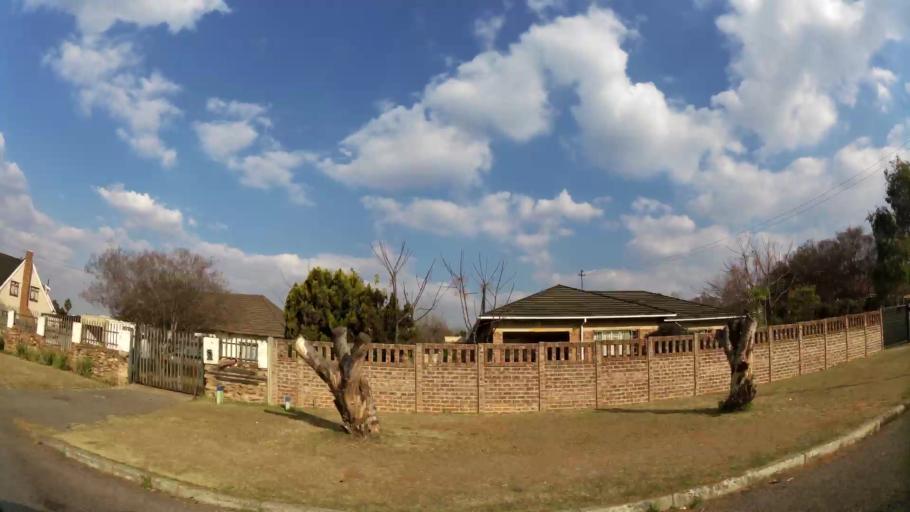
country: ZA
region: Gauteng
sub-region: Ekurhuleni Metropolitan Municipality
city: Germiston
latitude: -26.2305
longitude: 28.1798
